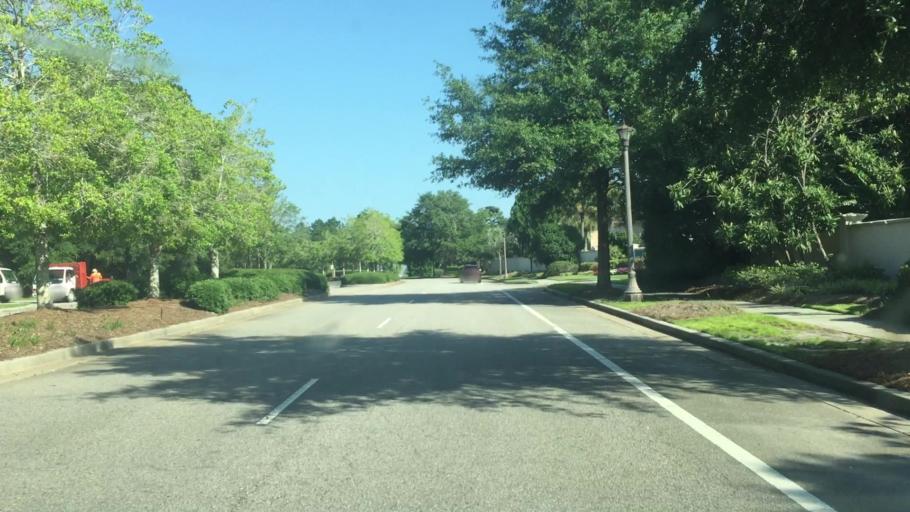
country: US
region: South Carolina
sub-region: Horry County
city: Myrtle Beach
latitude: 33.7505
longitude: -78.8126
